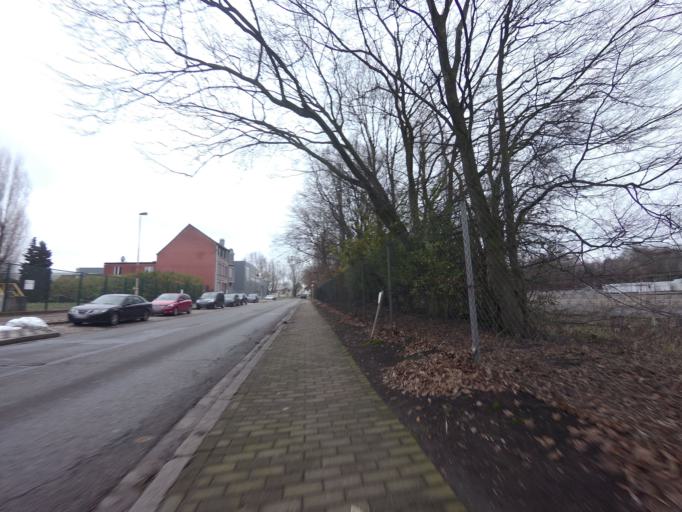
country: BE
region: Flanders
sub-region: Provincie Antwerpen
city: Hemiksem
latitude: 51.1581
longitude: 4.3422
